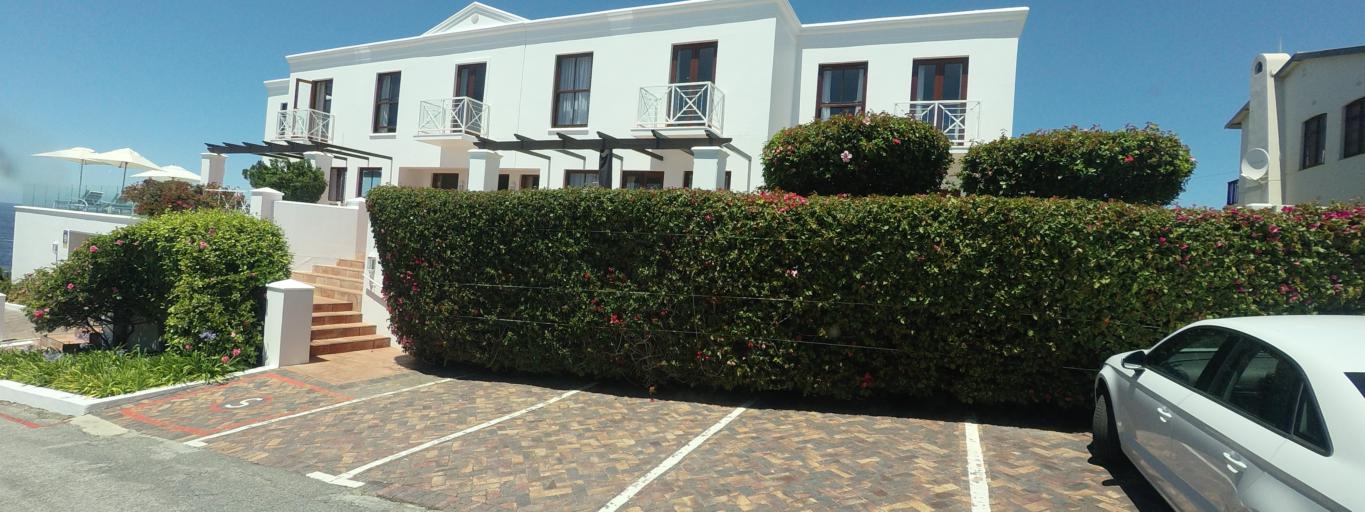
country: ZA
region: Western Cape
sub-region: Eden District Municipality
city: Plettenberg Bay
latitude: -34.0541
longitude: 23.3776
